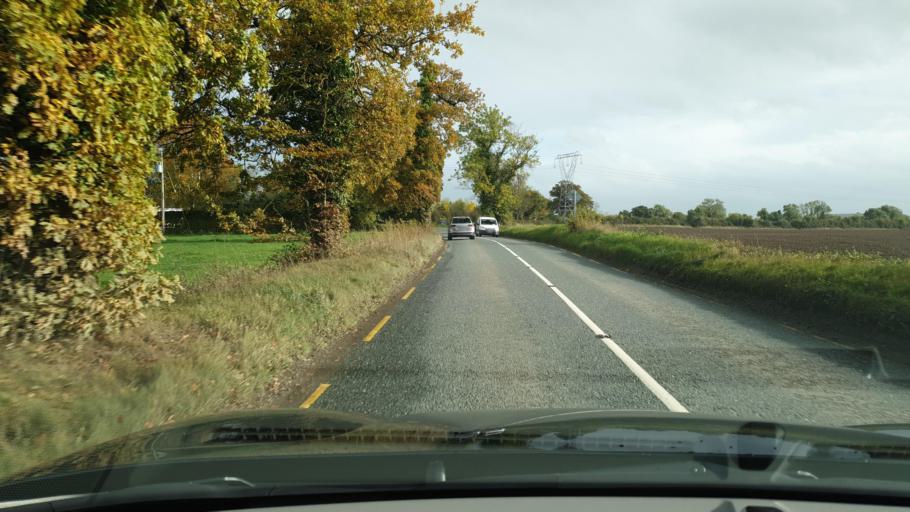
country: IE
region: Leinster
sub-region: An Mhi
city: Ratoath
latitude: 53.5141
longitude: -6.4849
